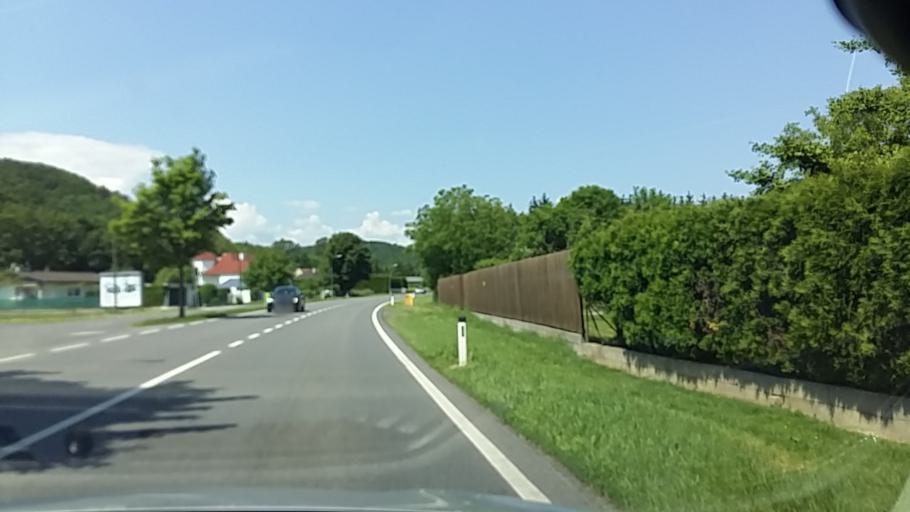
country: AT
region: Burgenland
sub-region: Politischer Bezirk Oberpullendorf
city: Oberpullendorf
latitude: 47.4843
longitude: 16.4790
